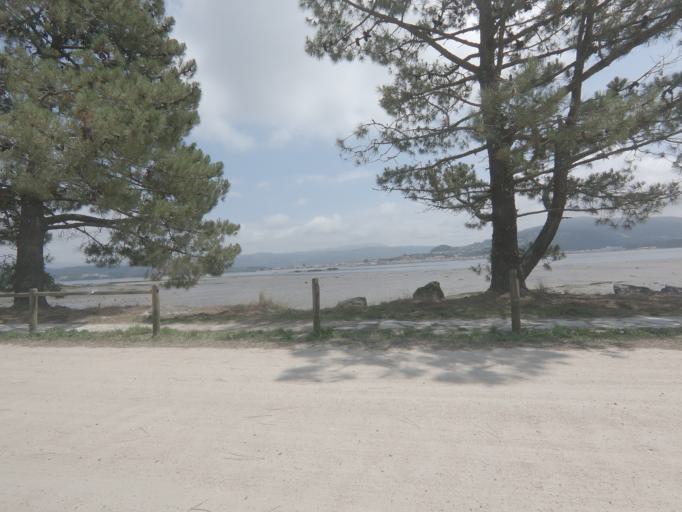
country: ES
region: Galicia
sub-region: Provincia de Pontevedra
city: A Guarda
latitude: 41.8831
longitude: -8.8584
